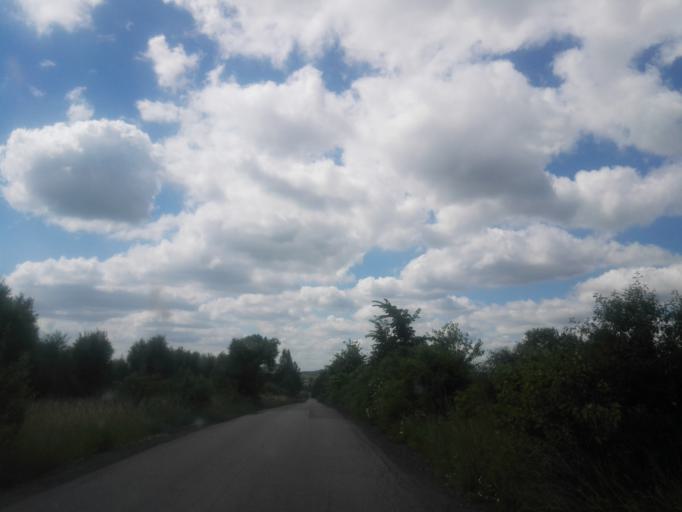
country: PL
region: Silesian Voivodeship
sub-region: Powiat czestochowski
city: Mstow
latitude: 50.8116
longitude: 19.2583
